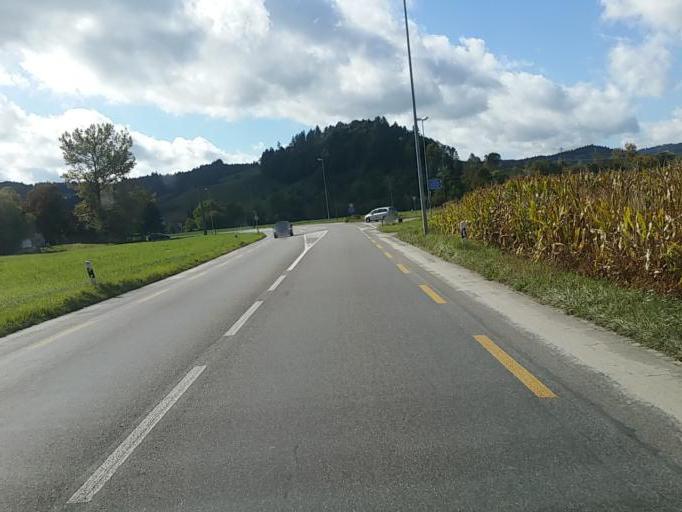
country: CH
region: Bern
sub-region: Oberaargau
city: Madiswil
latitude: 47.1505
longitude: 7.7888
